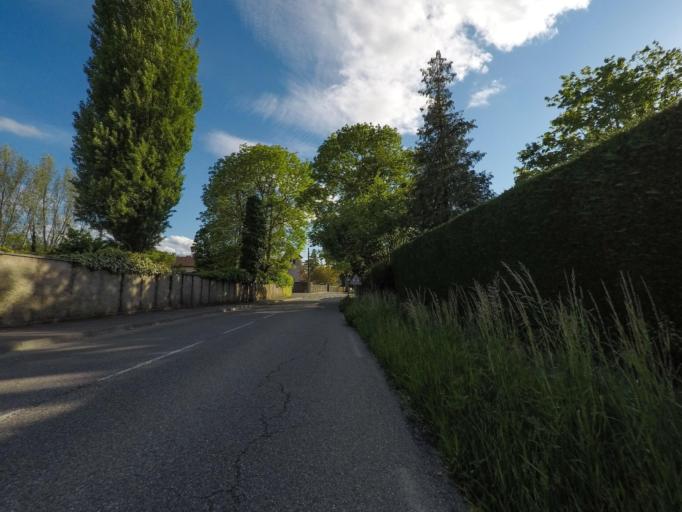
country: FR
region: Rhone-Alpes
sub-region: Departement de l'Ain
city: Saint-Genis-Pouilly
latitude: 46.2562
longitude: 6.0377
